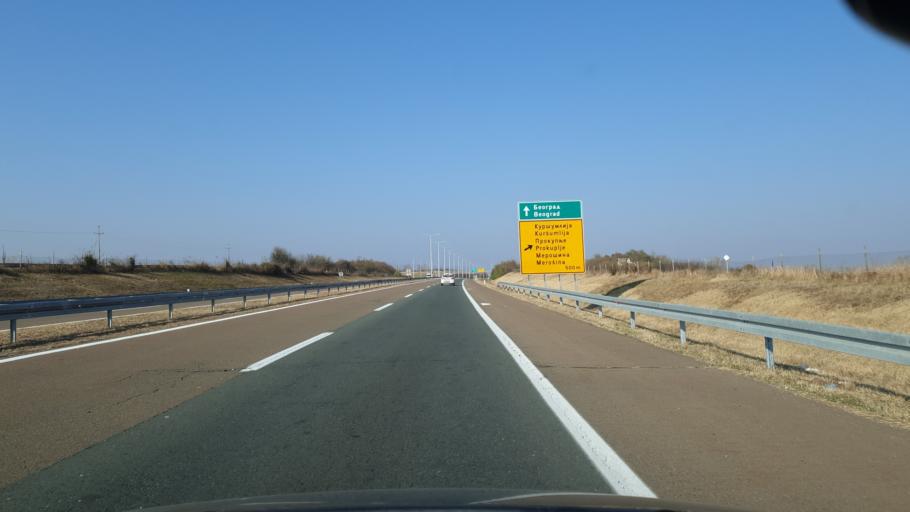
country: RS
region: Central Serbia
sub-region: Nisavski Okrug
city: Doljevac
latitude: 43.2746
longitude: 21.8049
